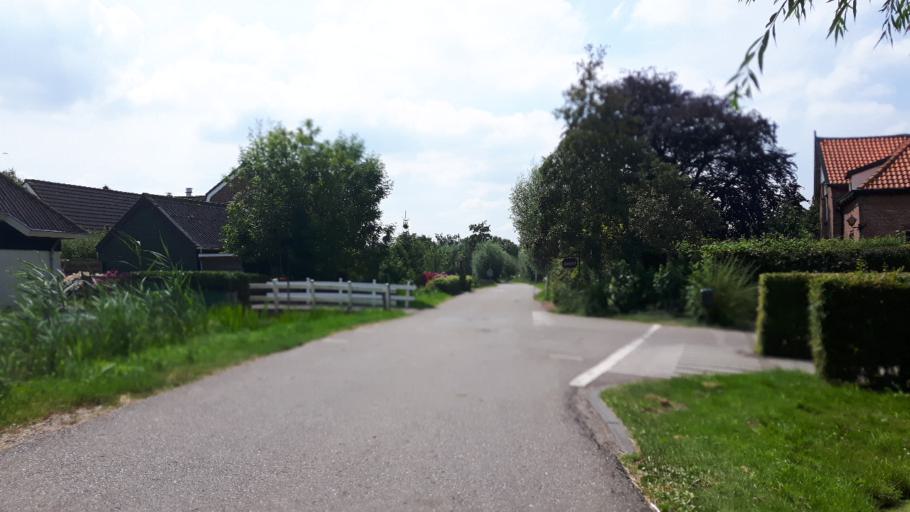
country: NL
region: South Holland
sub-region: Gemeente Giessenlanden
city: Giessenburg
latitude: 51.9036
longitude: 4.9007
